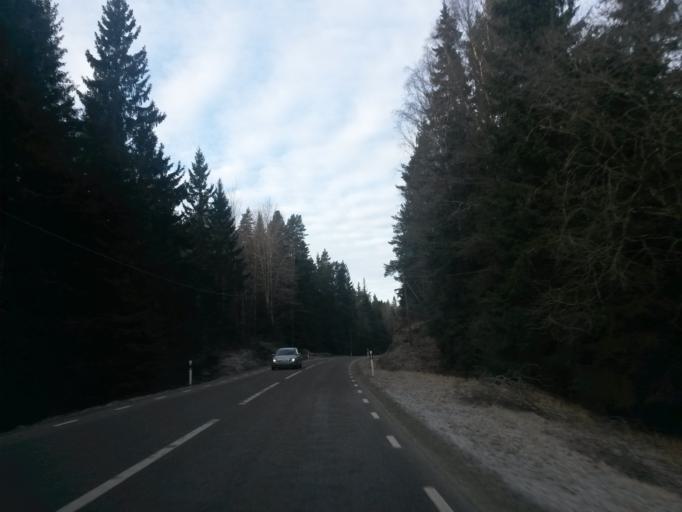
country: SE
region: Vaestra Goetaland
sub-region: Boras Kommun
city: Boras
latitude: 57.8483
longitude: 12.9522
